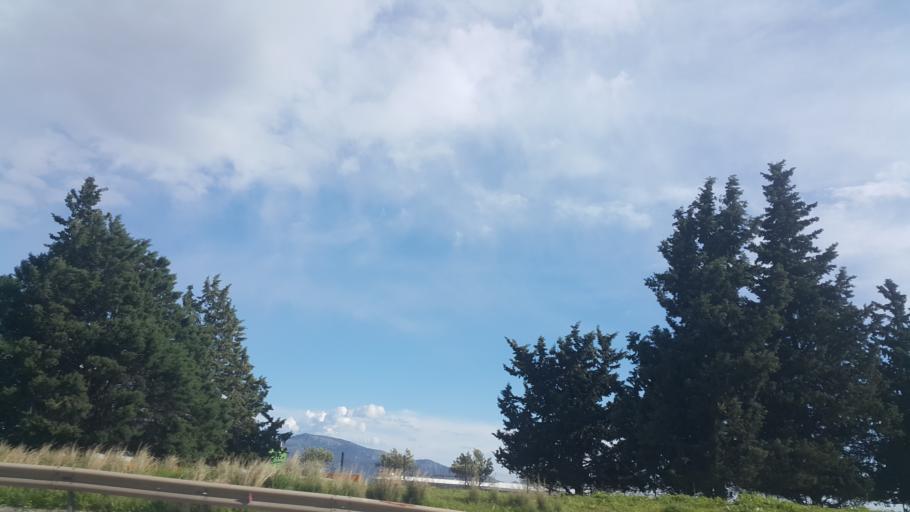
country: TR
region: Adana
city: Yakapinar
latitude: 36.9904
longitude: 35.6161
